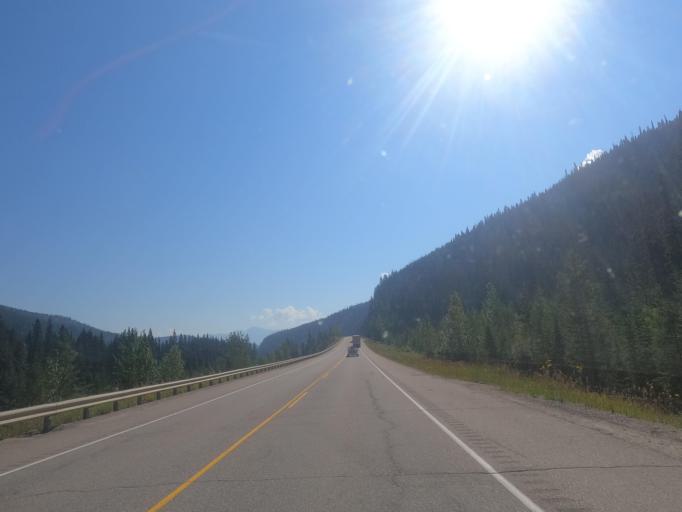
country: CA
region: Alberta
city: Jasper Park Lodge
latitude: 52.8754
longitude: -118.3135
